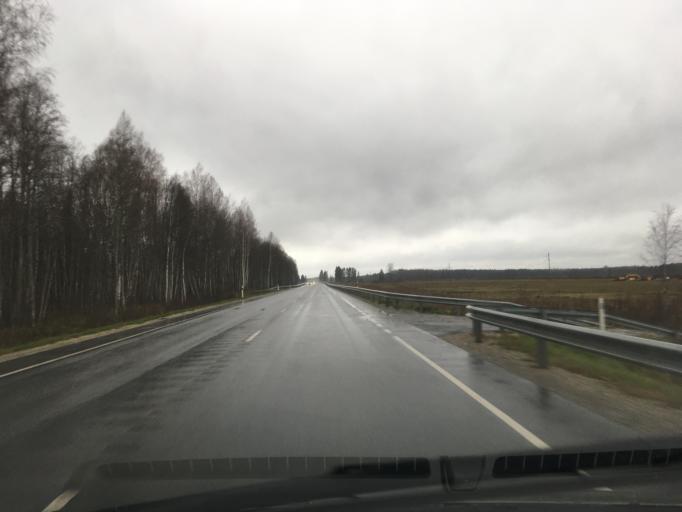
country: EE
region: Laeaene
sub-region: Lihula vald
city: Lihula
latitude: 58.7862
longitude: 24.0153
